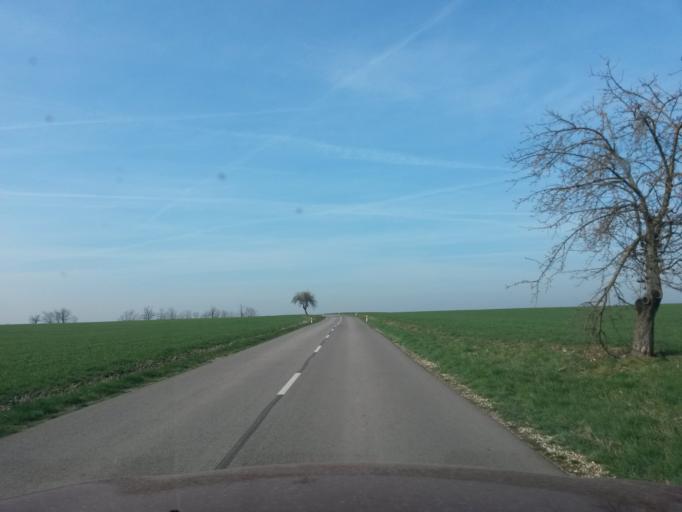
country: SK
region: Nitriansky
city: Svodin
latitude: 47.9816
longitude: 18.3894
